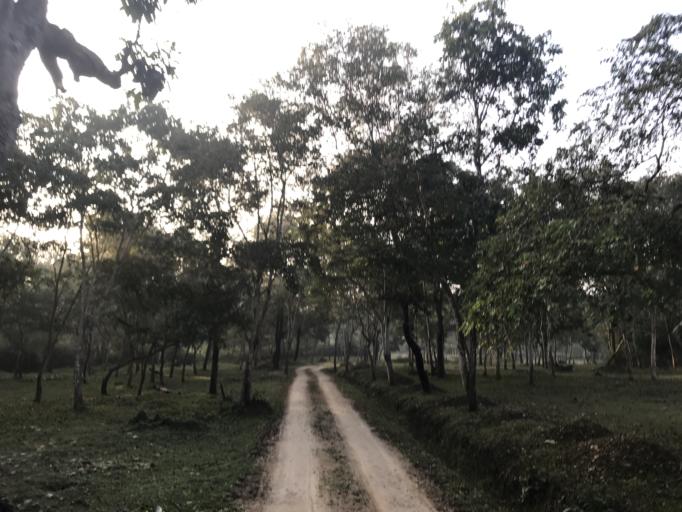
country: IN
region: Karnataka
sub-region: Mysore
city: Heggadadevankote
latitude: 12.0094
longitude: 76.2450
